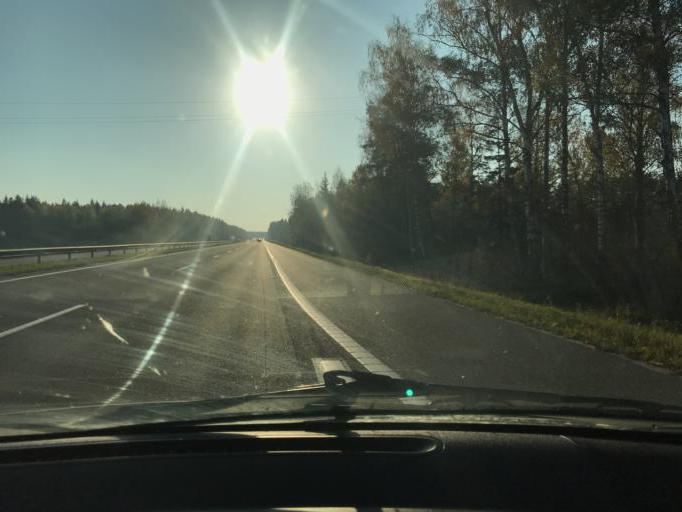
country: BY
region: Minsk
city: Loshnitsa
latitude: 54.2824
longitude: 28.7375
